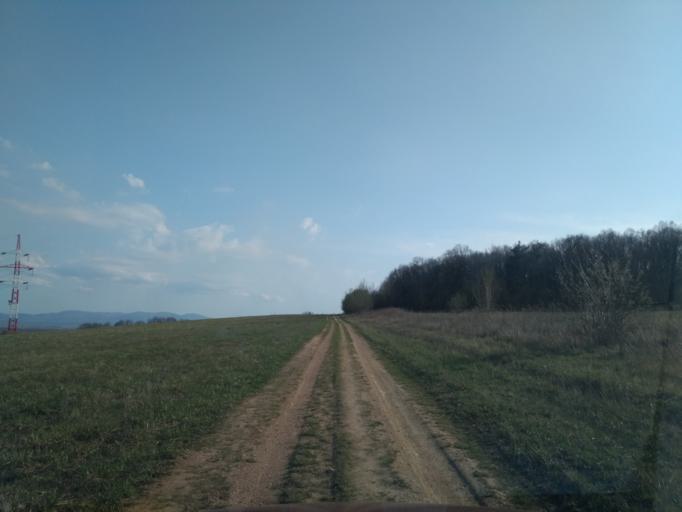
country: SK
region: Kosicky
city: Kosice
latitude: 48.6819
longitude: 21.1812
